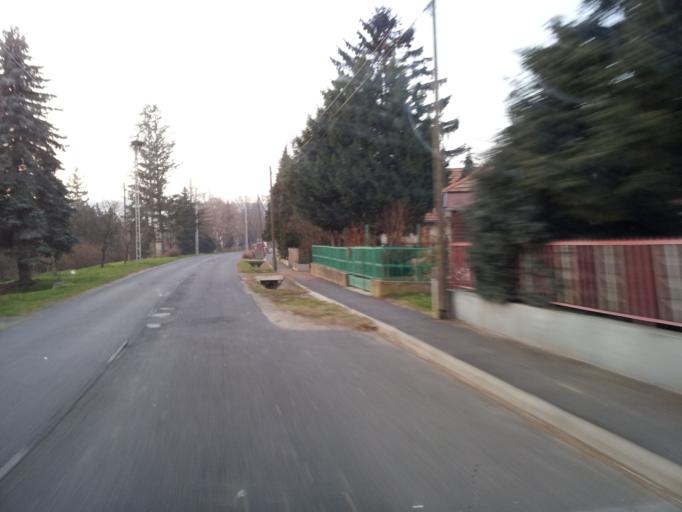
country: HU
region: Zala
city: Heviz
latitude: 46.8347
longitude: 17.1774
